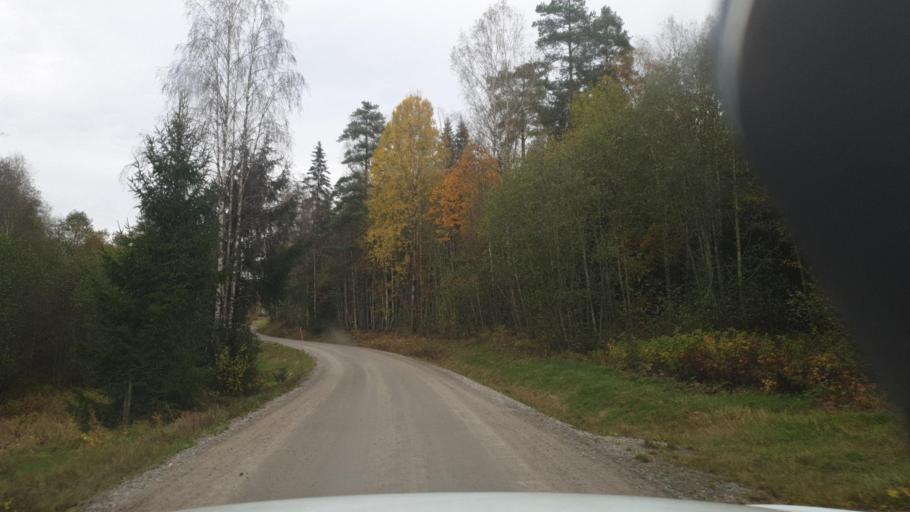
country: SE
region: Vaermland
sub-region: Arvika Kommun
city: Arvika
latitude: 59.6836
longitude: 12.7721
